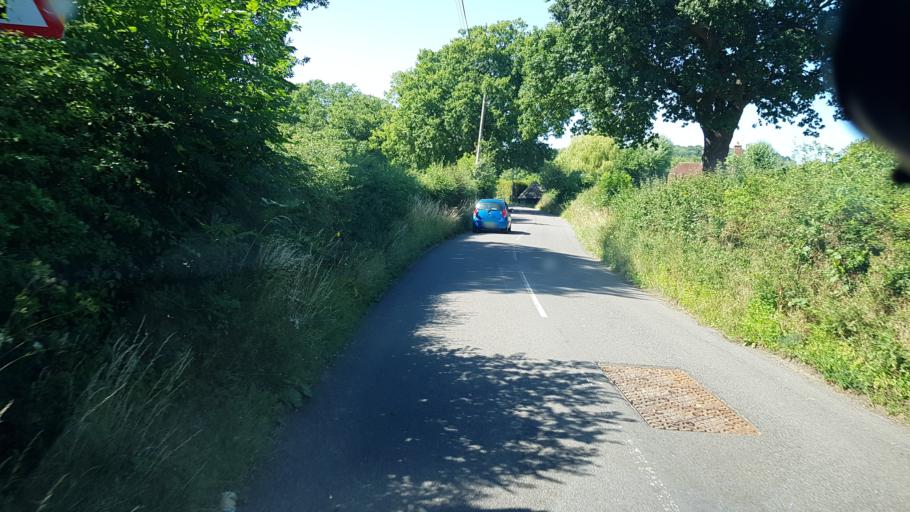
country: GB
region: England
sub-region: Kent
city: Westerham
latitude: 51.2291
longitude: 0.0719
